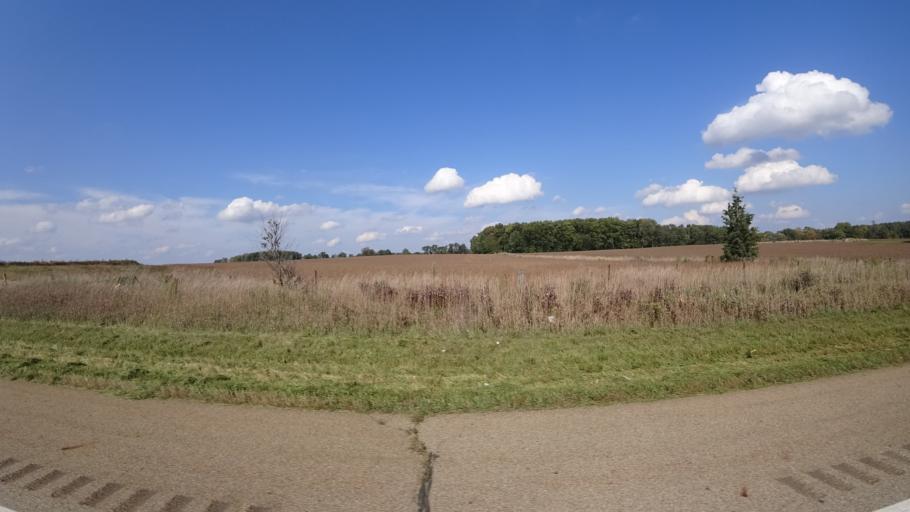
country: US
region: Michigan
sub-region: Calhoun County
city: Homer
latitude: 42.1619
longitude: -84.7364
